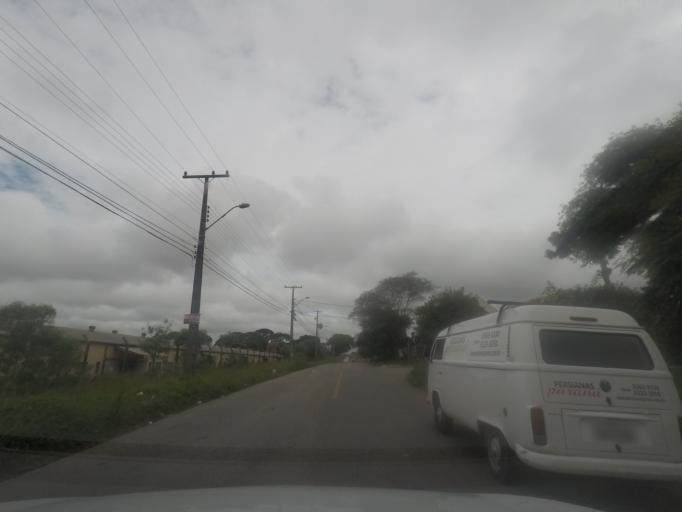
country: BR
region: Parana
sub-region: Pinhais
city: Pinhais
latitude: -25.4415
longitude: -49.2244
